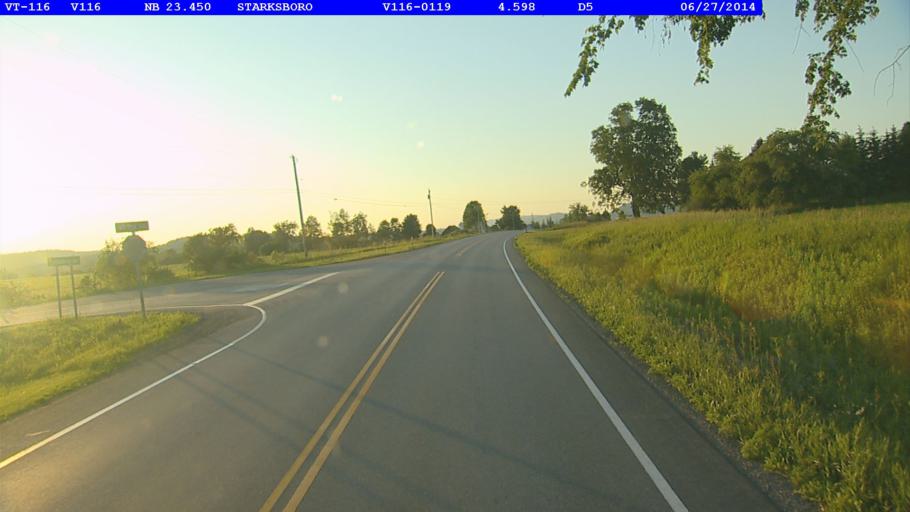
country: US
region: Vermont
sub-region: Chittenden County
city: Hinesburg
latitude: 44.2504
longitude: -73.0623
